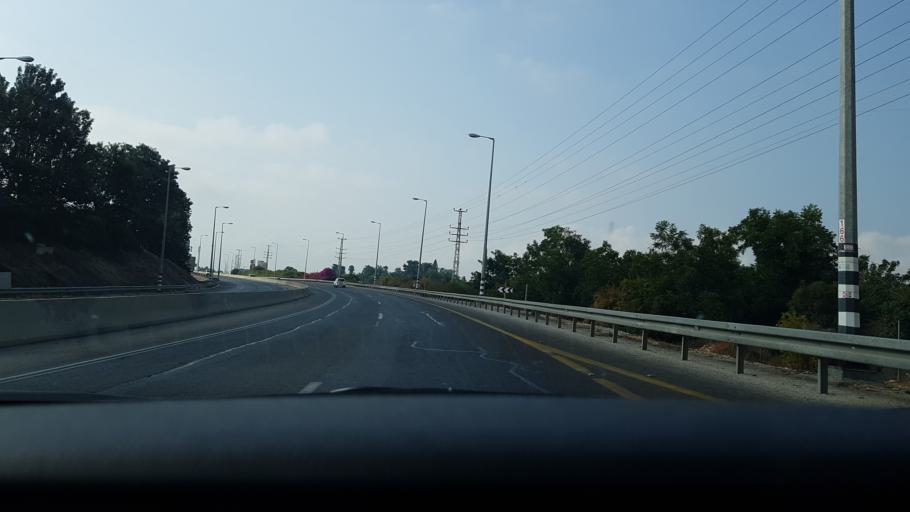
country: IL
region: Central District
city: Ness Ziona
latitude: 31.9433
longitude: 34.7805
